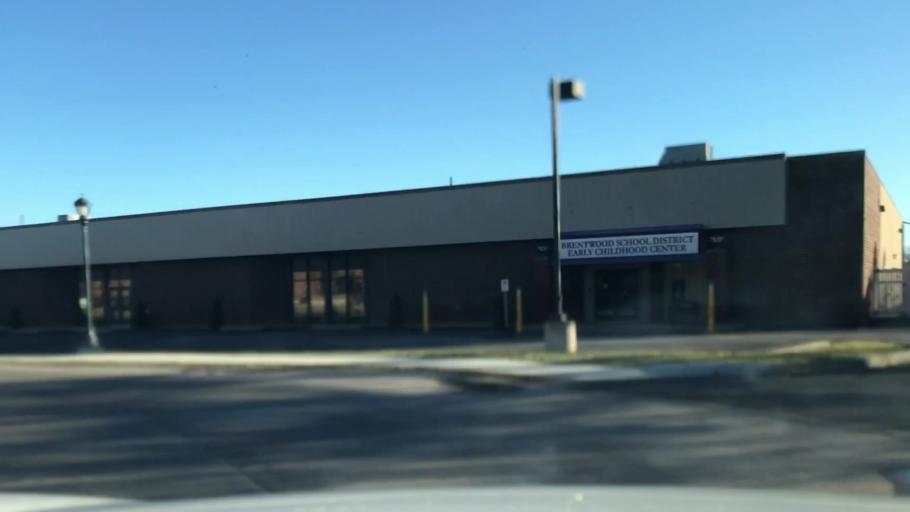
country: US
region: Missouri
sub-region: Saint Louis County
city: Brentwood
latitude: 38.6242
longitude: -90.3397
